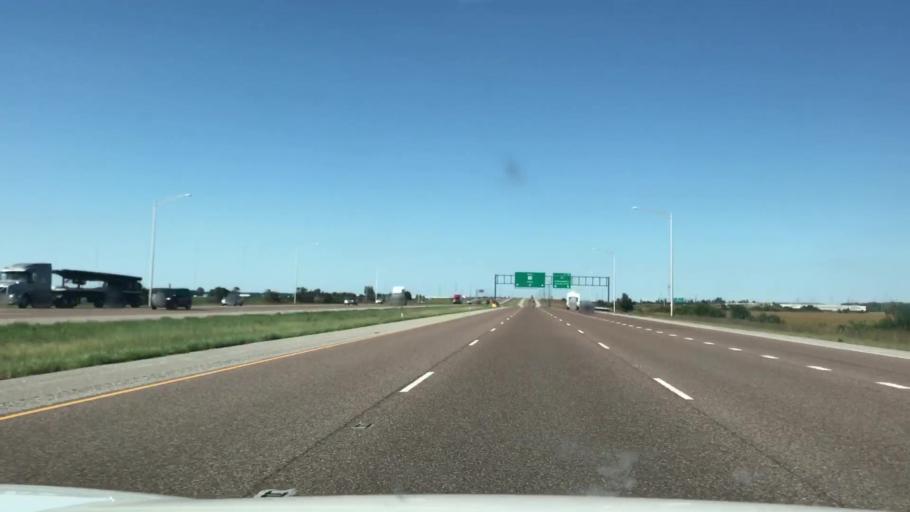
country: US
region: Illinois
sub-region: Madison County
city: Pontoon Beach
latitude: 38.7469
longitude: -90.0434
